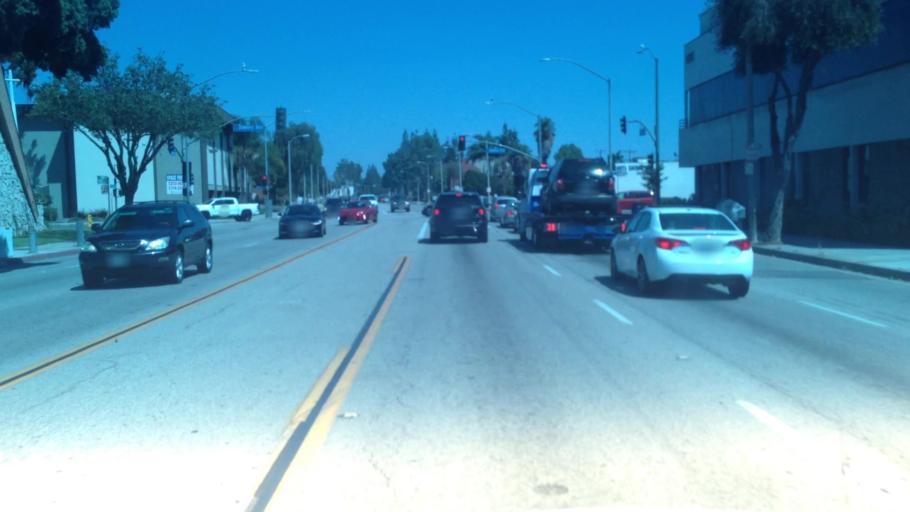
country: US
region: California
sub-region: Los Angeles County
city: Downey
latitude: 33.9518
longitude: -118.1265
